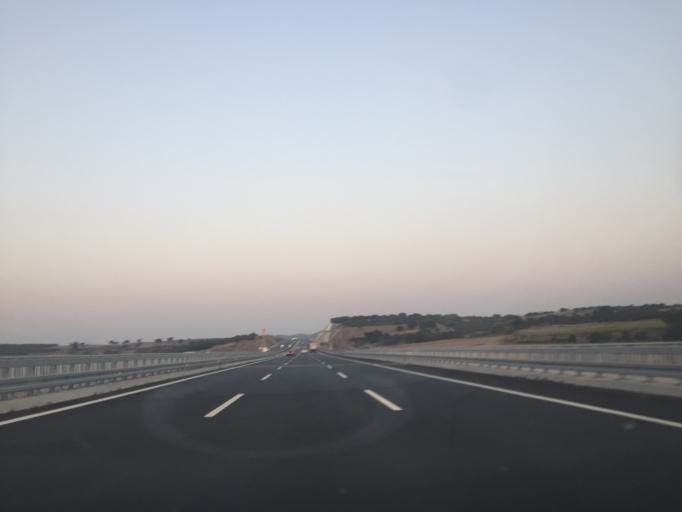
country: TR
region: Bursa
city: Mahmudiye
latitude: 40.2633
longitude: 28.6675
